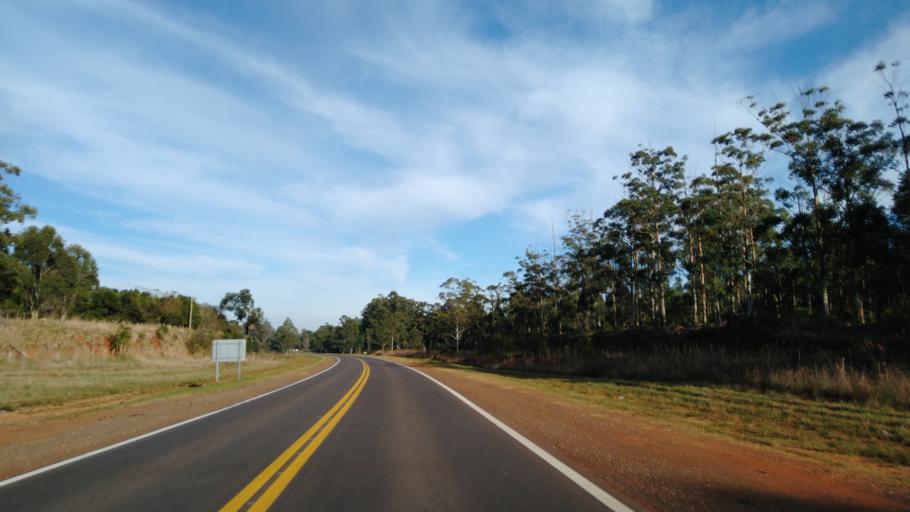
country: AR
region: Corrientes
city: Yapeyu
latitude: -29.4244
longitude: -56.8588
